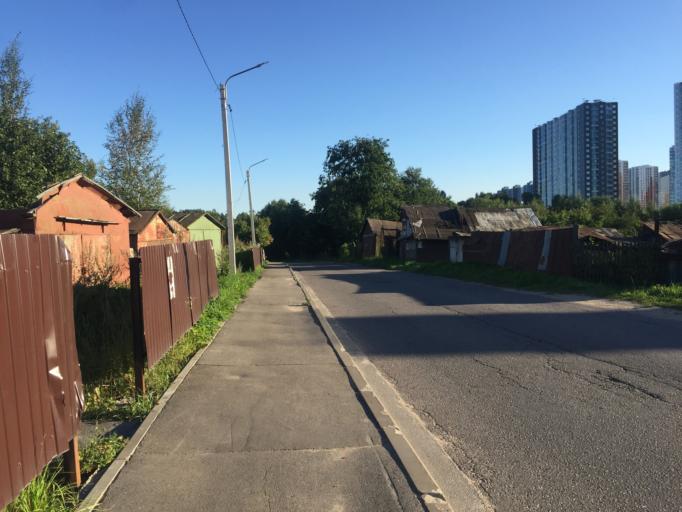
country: RU
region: Leningrad
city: Murino
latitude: 60.0361
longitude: 30.4653
